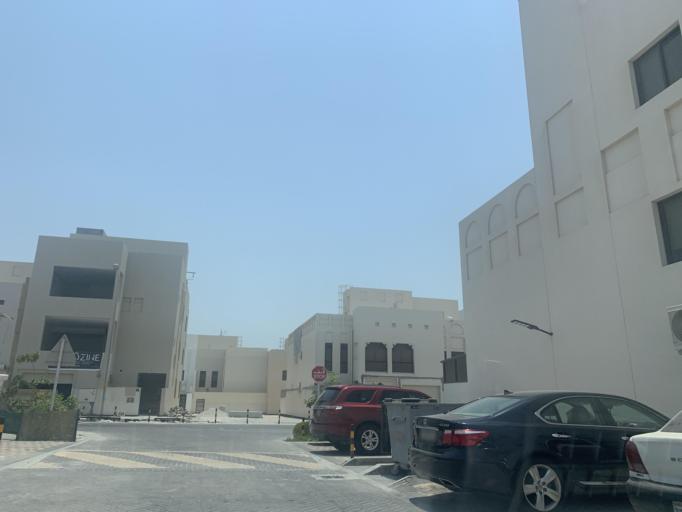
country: BH
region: Muharraq
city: Al Hadd
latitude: 26.2336
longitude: 50.6707
